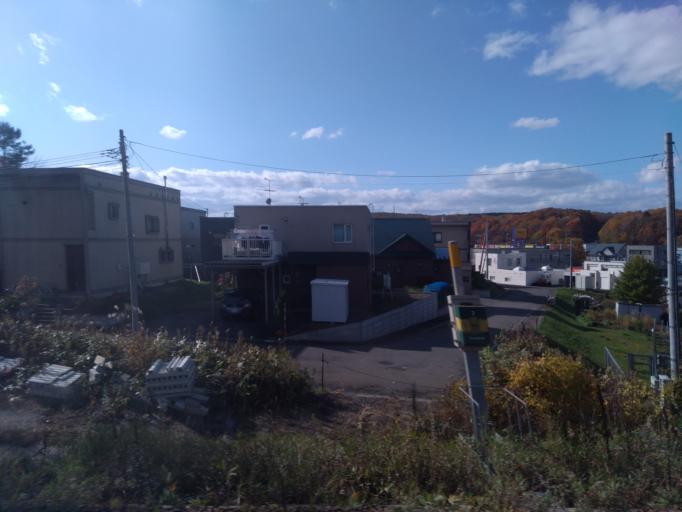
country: JP
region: Hokkaido
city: Kitahiroshima
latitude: 42.9844
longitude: 141.5624
